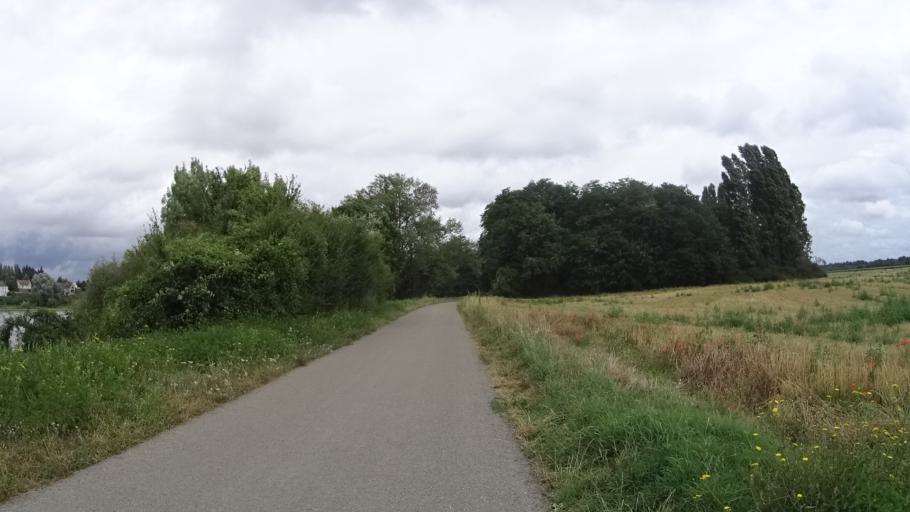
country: FR
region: Centre
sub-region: Departement du Loiret
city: Meung-sur-Loire
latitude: 47.8295
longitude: 1.7116
